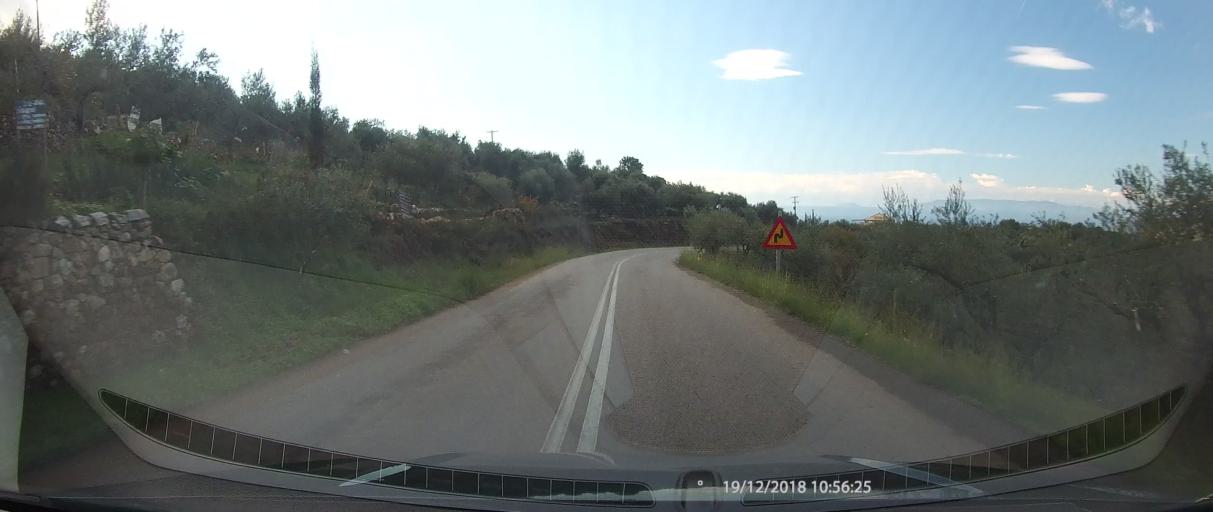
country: GR
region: Peloponnese
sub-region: Nomos Messinias
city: Kardamyli
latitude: 36.9015
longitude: 22.2405
